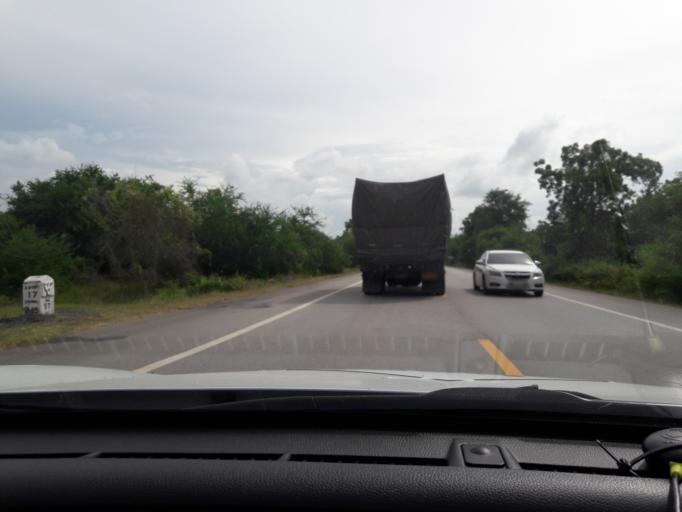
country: TH
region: Nakhon Sawan
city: Tak Fa
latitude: 15.4928
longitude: 100.5388
